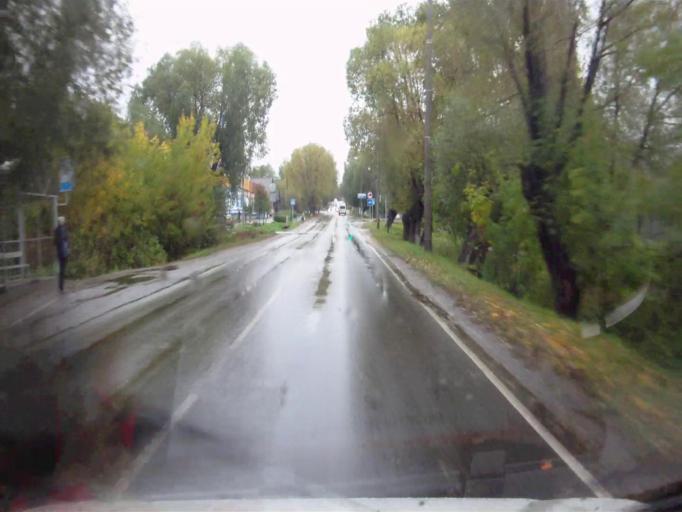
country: RU
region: Chelyabinsk
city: Kyshtym
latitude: 55.7189
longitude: 60.5425
